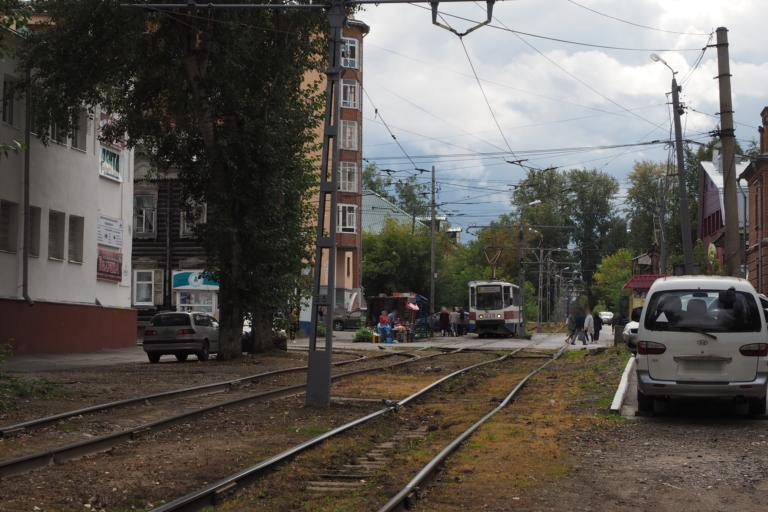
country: RU
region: Tomsk
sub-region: Tomskiy Rayon
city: Tomsk
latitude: 56.4799
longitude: 84.9530
